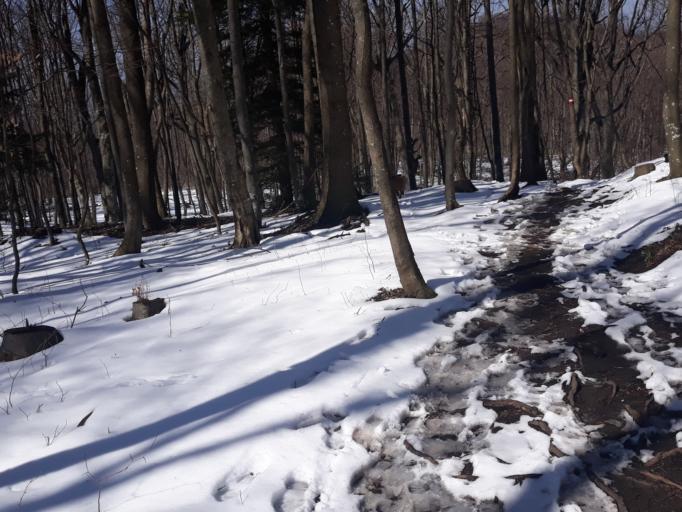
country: HR
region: Varazdinska
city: Ivanec
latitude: 46.1801
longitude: 16.1143
